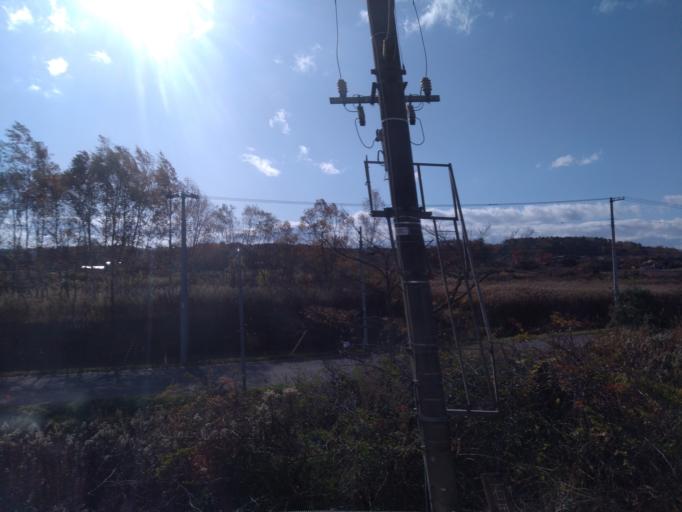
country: JP
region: Hokkaido
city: Kitahiroshima
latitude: 42.9915
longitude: 141.5550
